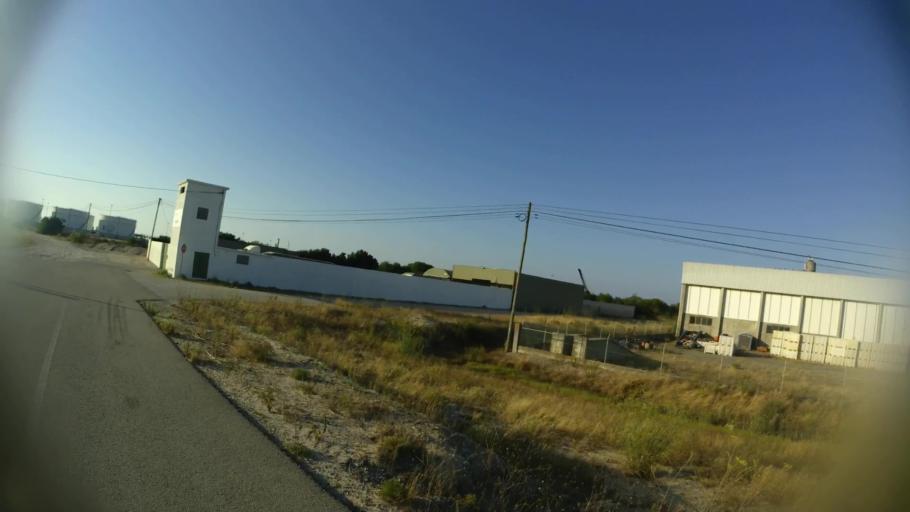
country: PT
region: Aveiro
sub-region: Ilhavo
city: Gafanha da Nazare
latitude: 40.6483
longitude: -8.7024
